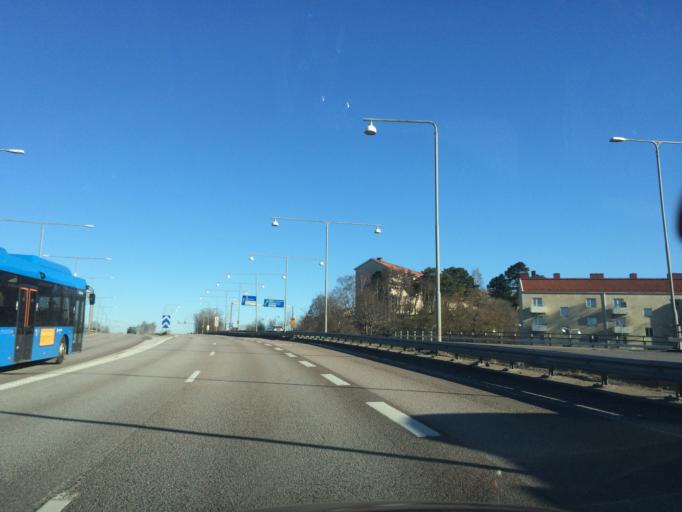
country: SE
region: Vaestra Goetaland
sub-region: Goteborg
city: Majorna
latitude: 57.6818
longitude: 11.9049
